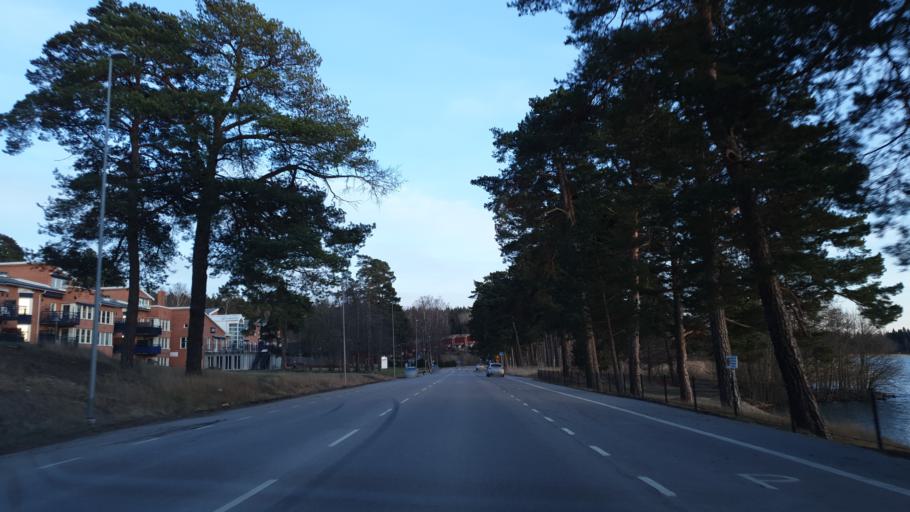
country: SE
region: Uppsala
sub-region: Habo Kommun
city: Balsta
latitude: 59.5522
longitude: 17.5549
